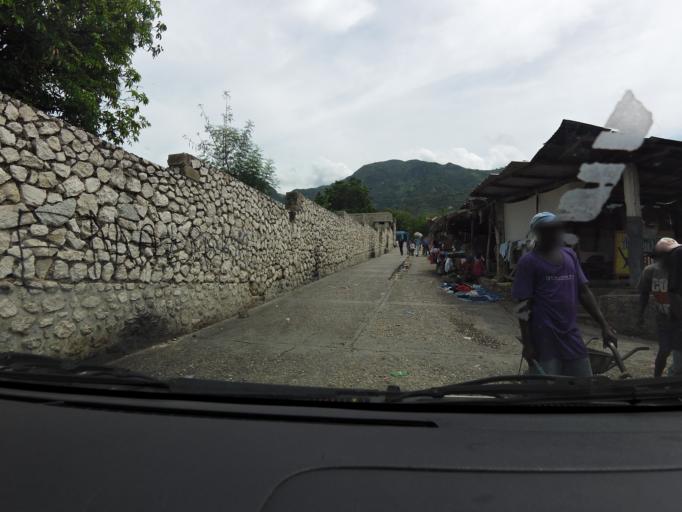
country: HT
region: Artibonite
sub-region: Arrondissement de Saint-Marc
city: Verrettes
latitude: 18.8892
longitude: -72.6226
